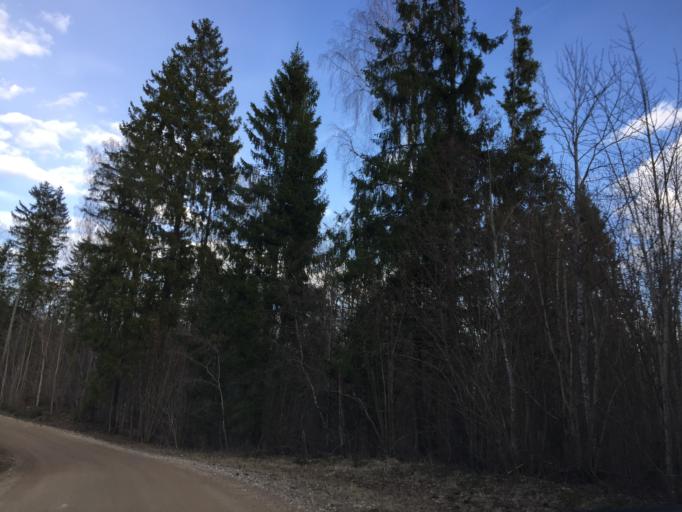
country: EE
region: Tartu
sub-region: Noo vald
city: Noo
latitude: 58.1328
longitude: 26.6028
